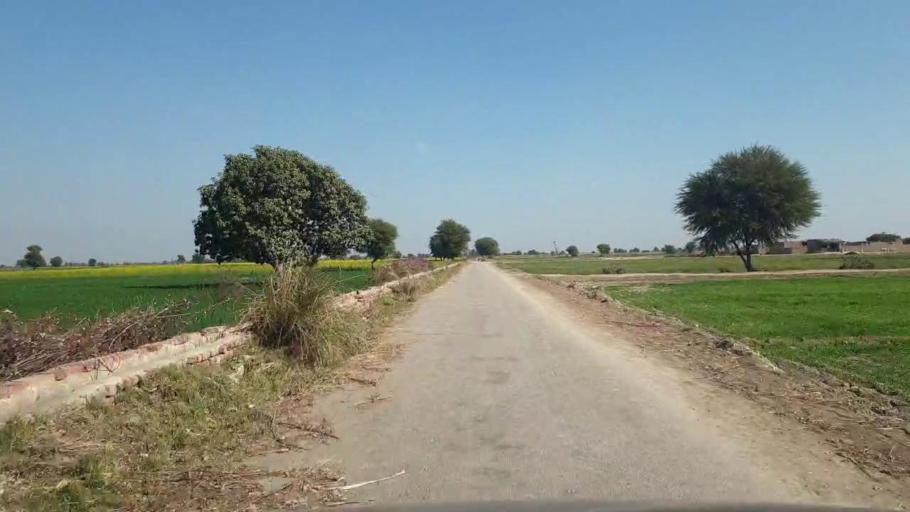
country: PK
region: Sindh
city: Shahpur Chakar
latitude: 26.1079
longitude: 68.6613
